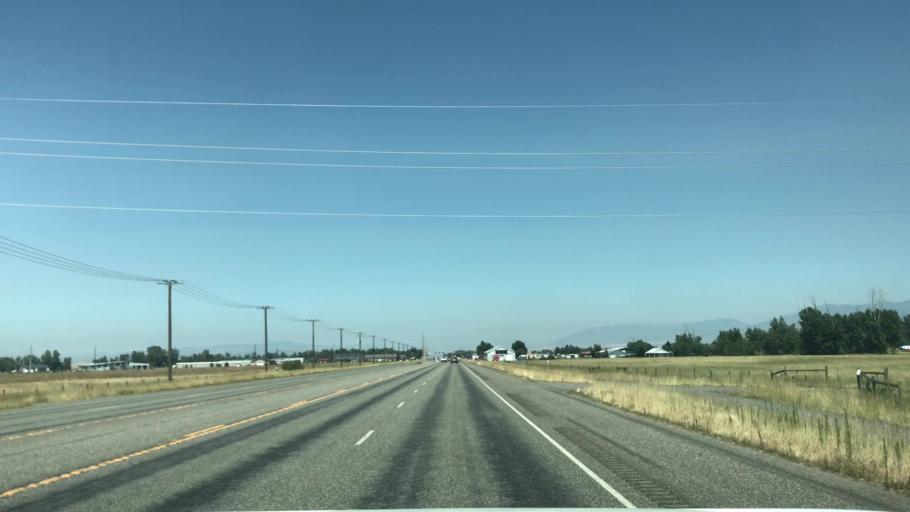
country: US
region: Montana
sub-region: Gallatin County
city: Four Corners
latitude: 45.6924
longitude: -111.1855
